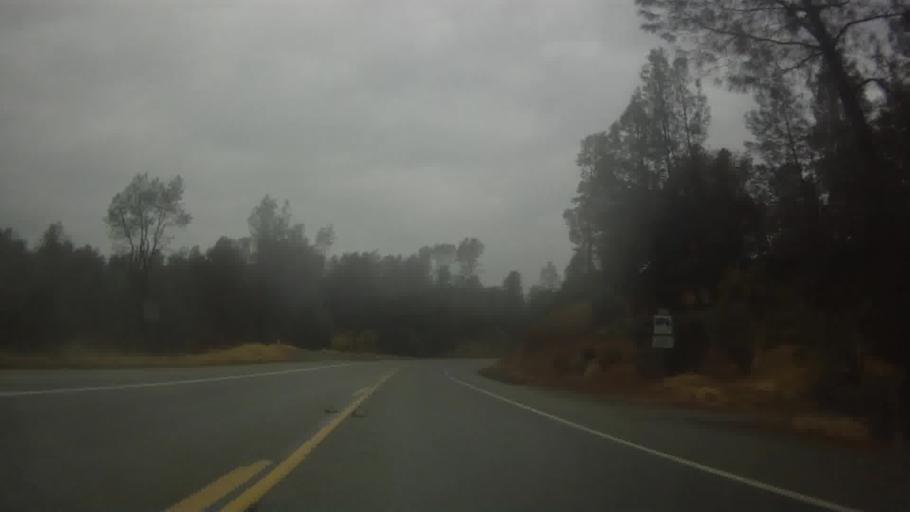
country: US
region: California
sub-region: Shasta County
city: Shasta
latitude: 40.5864
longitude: -122.4545
